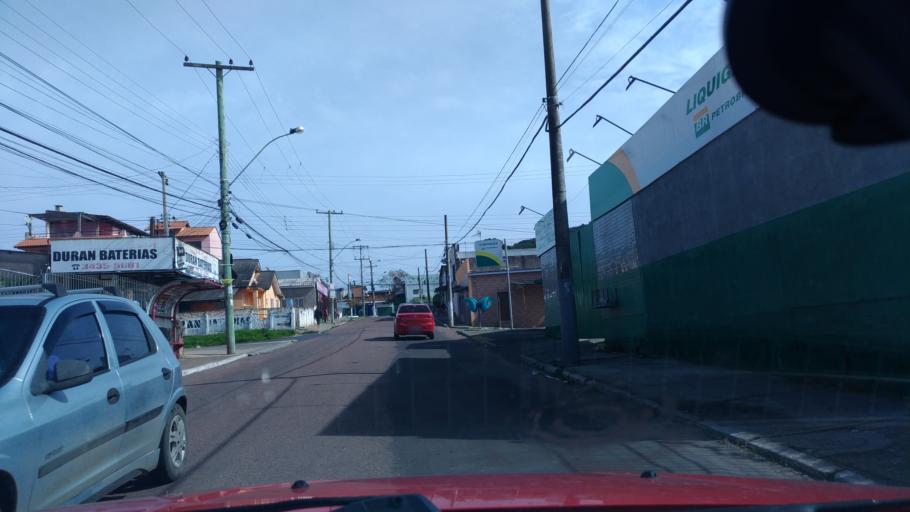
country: BR
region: Rio Grande do Sul
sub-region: Viamao
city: Viamao
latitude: -30.0617
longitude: -51.1069
